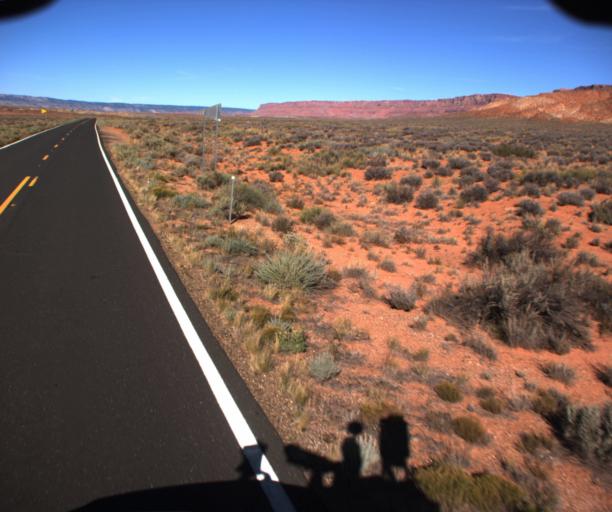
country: US
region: Arizona
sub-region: Coconino County
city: Page
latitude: 36.6843
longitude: -111.8562
